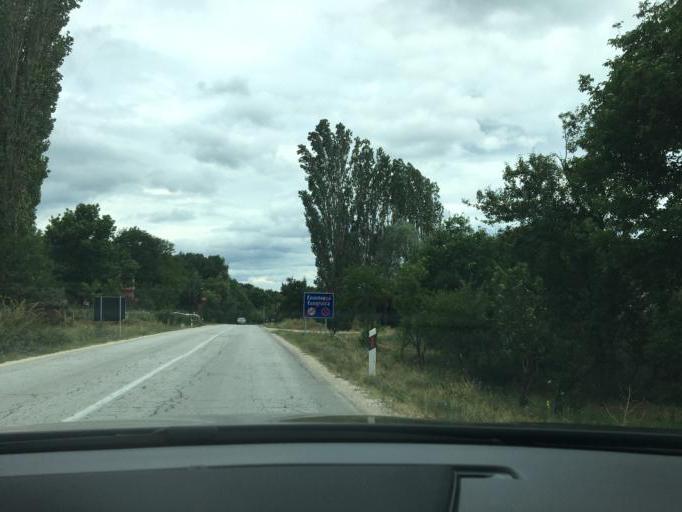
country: MK
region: Kriva Palanka
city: Kriva Palanka
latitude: 42.1769
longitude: 22.2581
